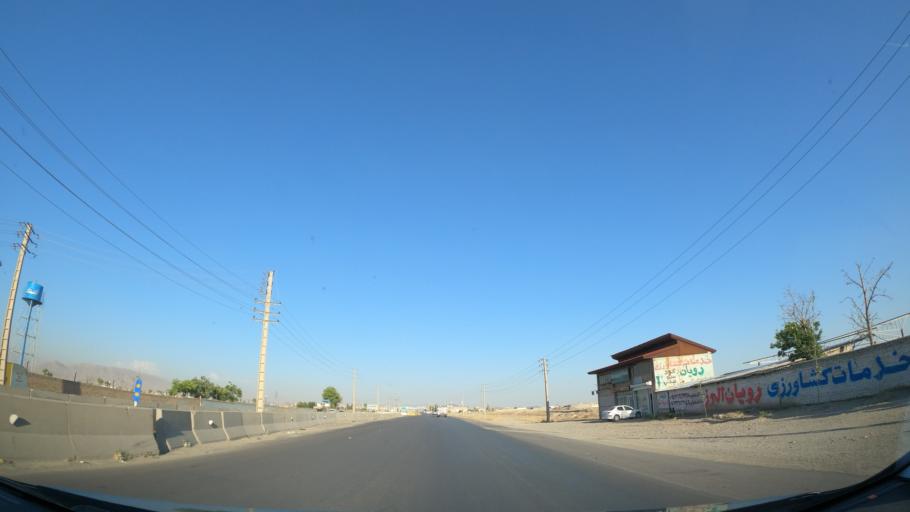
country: IR
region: Alborz
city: Hashtgerd
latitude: 35.9208
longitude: 50.7471
